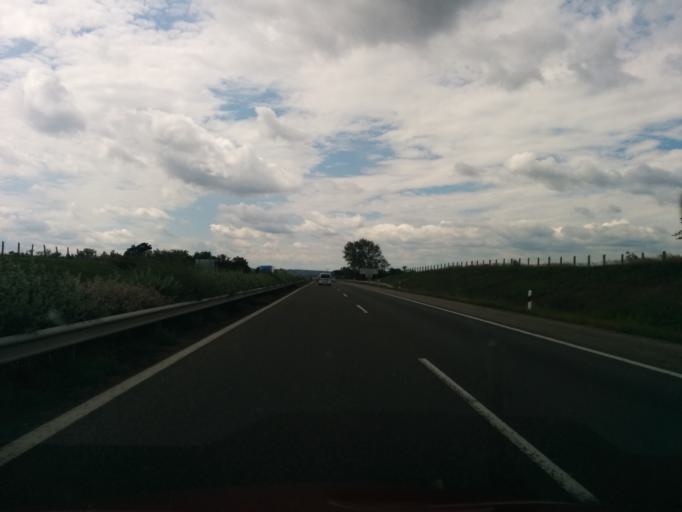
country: HU
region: Gyor-Moson-Sopron
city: Toltestava
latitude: 47.6542
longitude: 17.7243
